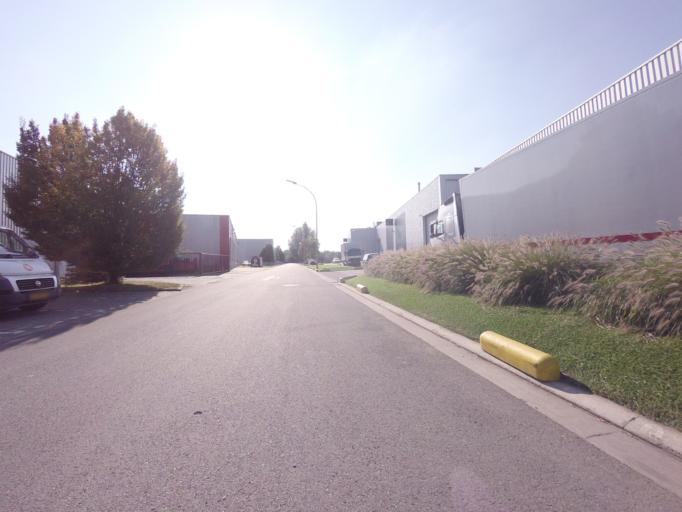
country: BE
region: Flanders
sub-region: Provincie Antwerpen
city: Willebroek
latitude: 51.0686
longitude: 4.3552
